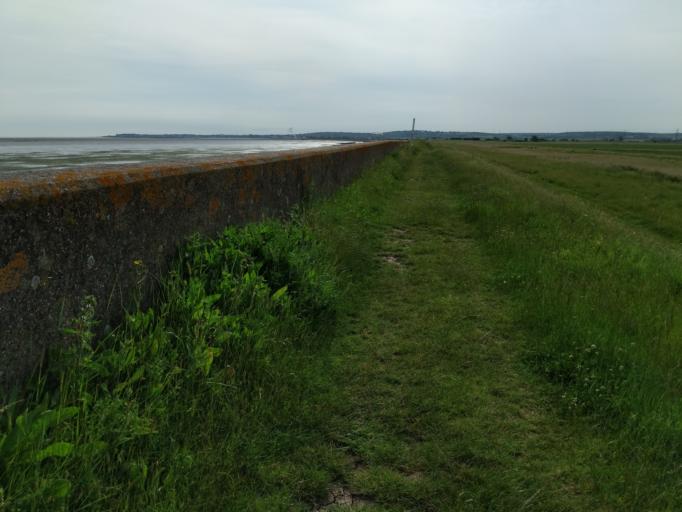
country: GB
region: England
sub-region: Kent
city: Leysdown-on-Sea
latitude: 51.3463
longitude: 0.9426
